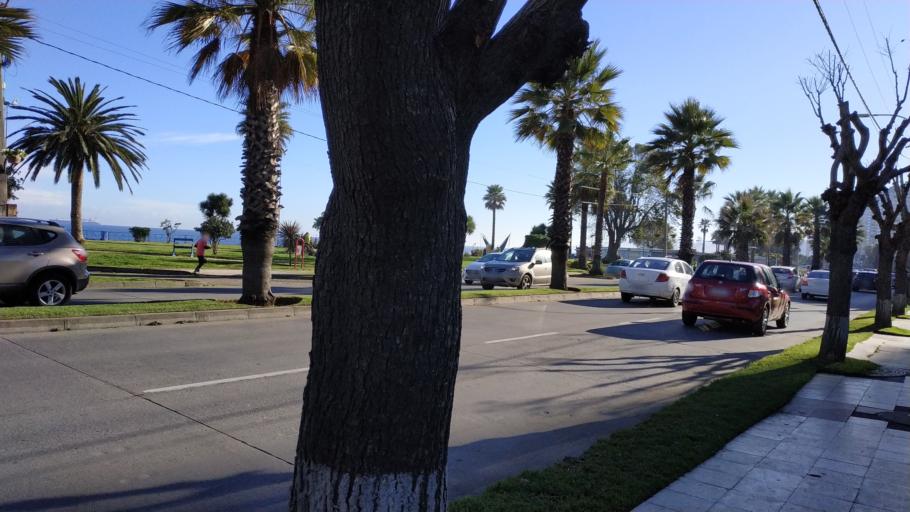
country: CL
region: Valparaiso
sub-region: Provincia de Valparaiso
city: Vina del Mar
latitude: -33.0118
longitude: -71.5530
